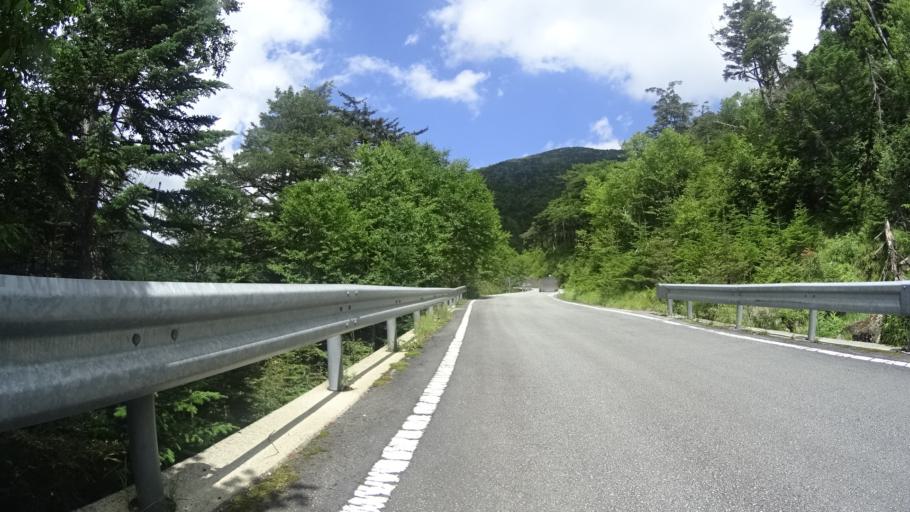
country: JP
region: Yamanashi
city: Enzan
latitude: 35.8671
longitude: 138.6632
